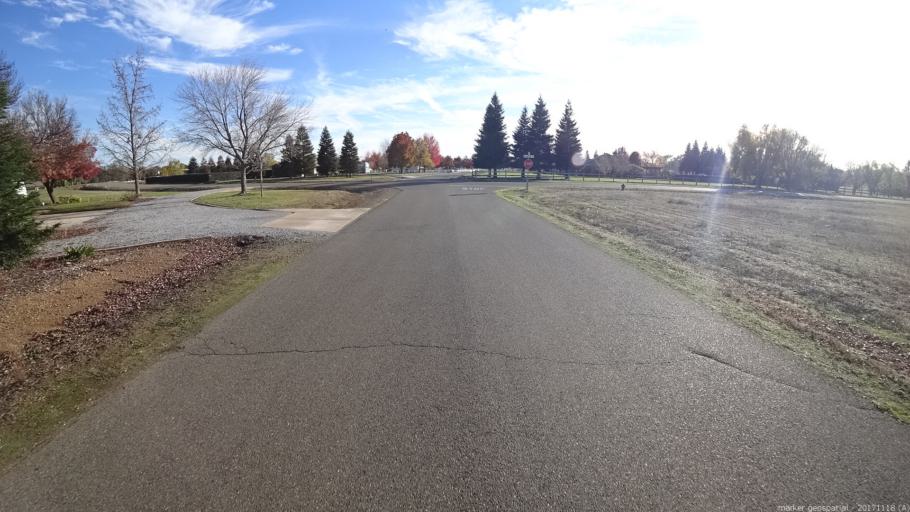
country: US
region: California
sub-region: Shasta County
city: Cottonwood
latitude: 40.3786
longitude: -122.3352
